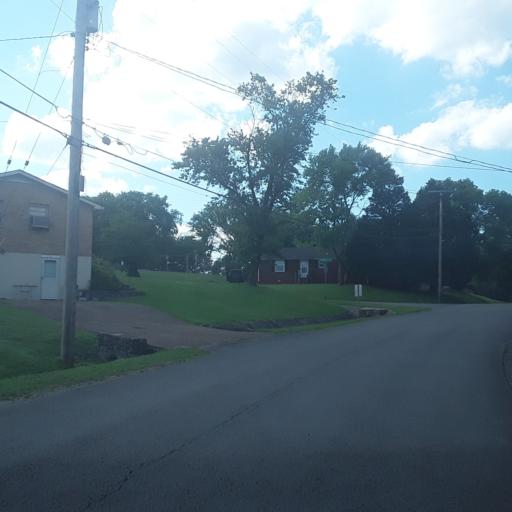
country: US
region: Tennessee
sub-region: Davidson County
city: Lakewood
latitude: 36.2018
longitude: -86.6280
